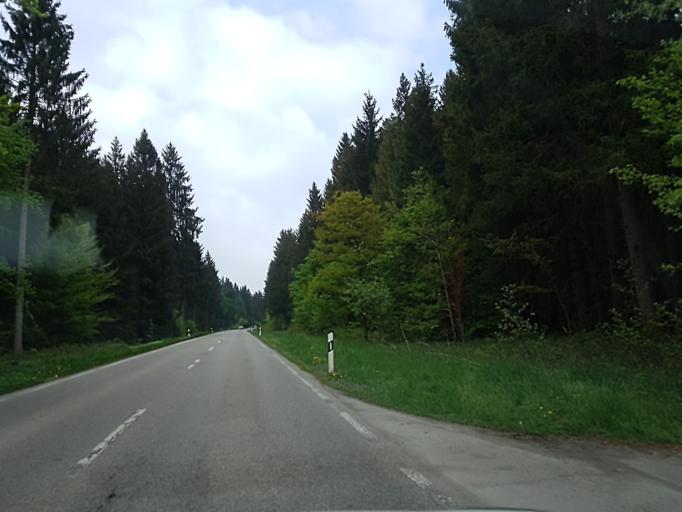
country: DE
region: Bavaria
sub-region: Upper Bavaria
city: Hohenlinden
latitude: 48.1288
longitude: 11.9806
